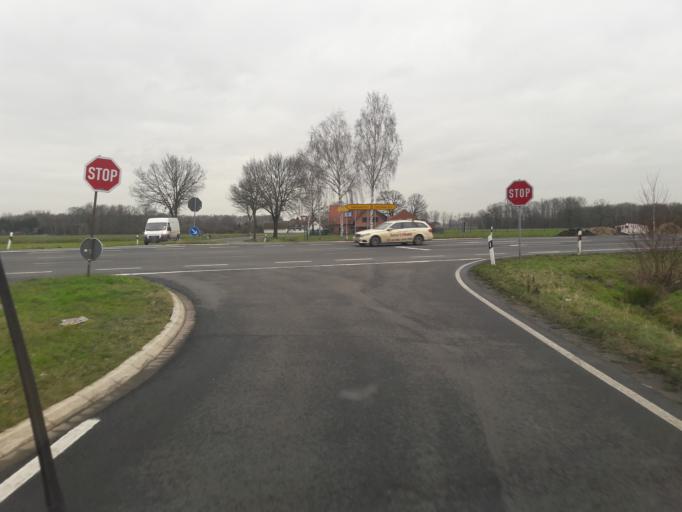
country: DE
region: Lower Saxony
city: Warmsen
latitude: 52.3868
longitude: 8.8517
